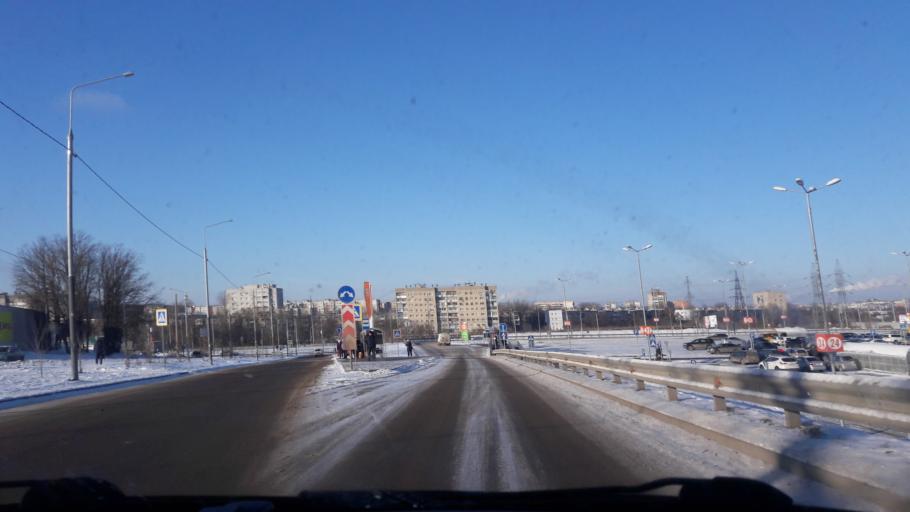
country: RU
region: Tula
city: Tula
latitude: 54.1748
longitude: 37.6462
